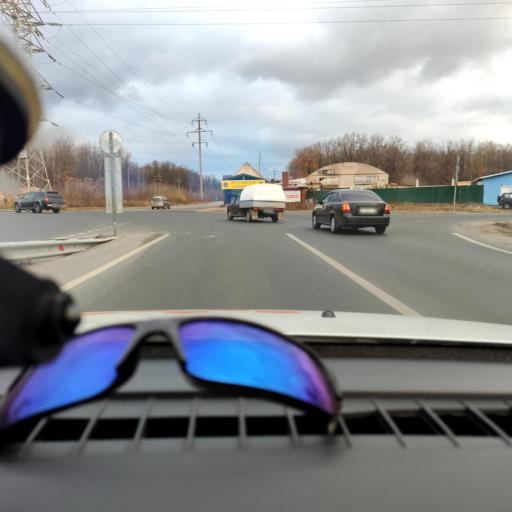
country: RU
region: Samara
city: Novosemeykino
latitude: 53.3479
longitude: 50.2336
